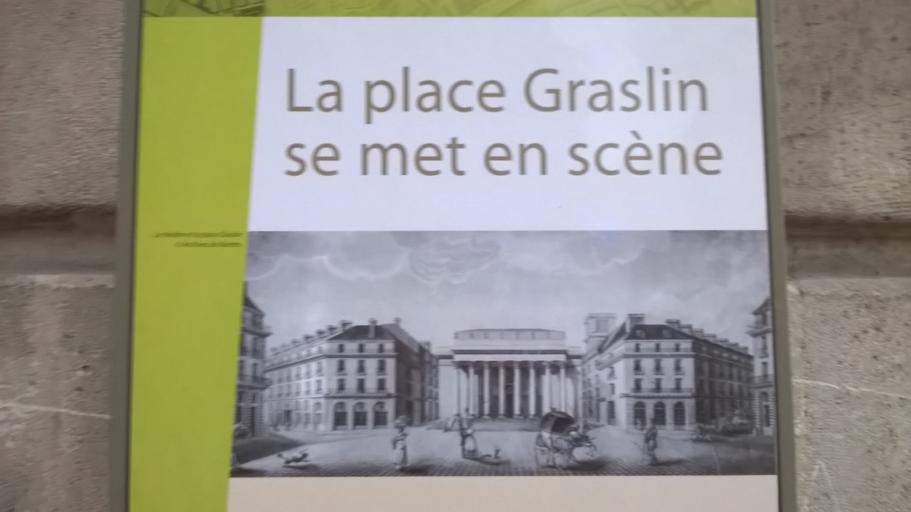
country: FR
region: Pays de la Loire
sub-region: Departement de la Loire-Atlantique
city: Nantes
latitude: 47.2129
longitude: -1.5609
